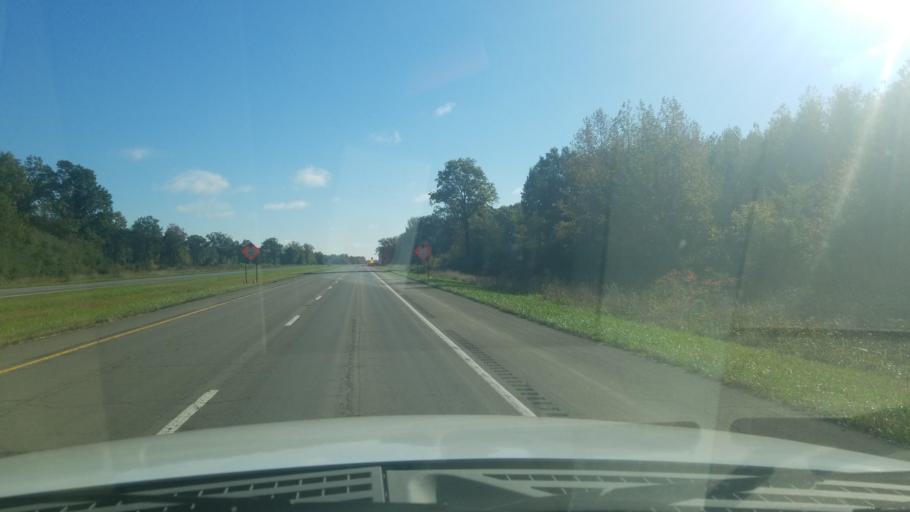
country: US
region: Illinois
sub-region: Saline County
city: Carrier Mills
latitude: 37.7334
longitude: -88.6587
